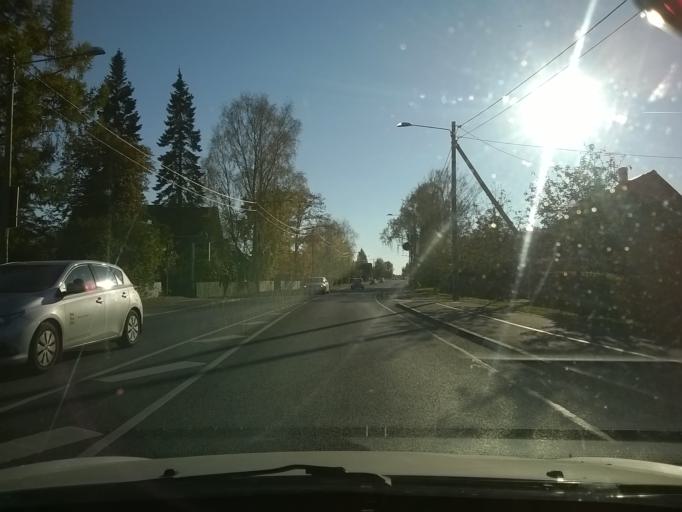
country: EE
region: Tartu
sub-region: Tartu linn
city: Tartu
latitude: 58.3544
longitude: 26.7210
